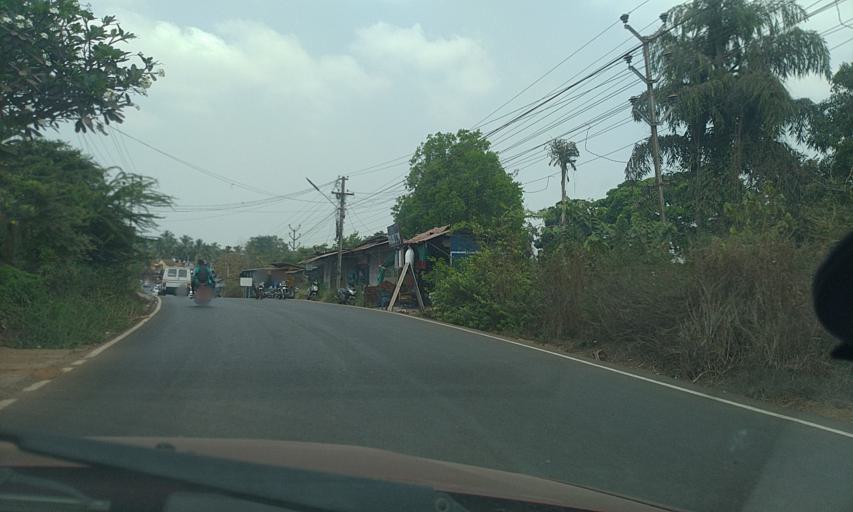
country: IN
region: Goa
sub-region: North Goa
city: Mapuca
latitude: 15.6018
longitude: 73.8067
